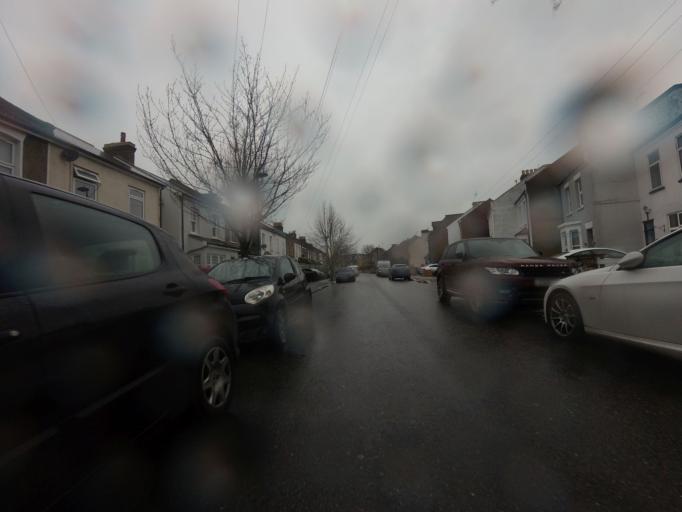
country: GB
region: England
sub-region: Hertfordshire
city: Waltham Cross
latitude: 51.6756
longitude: -0.0337
